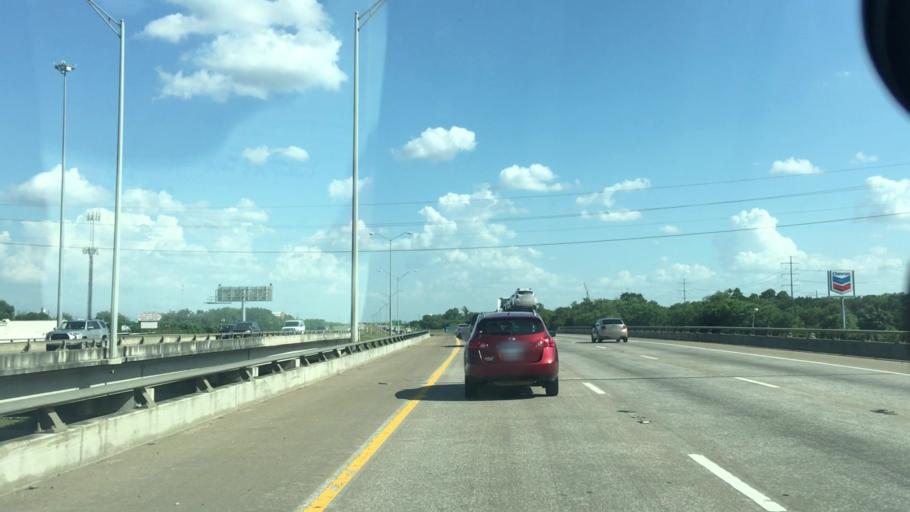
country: US
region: Texas
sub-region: Dallas County
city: Dallas
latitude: 32.7250
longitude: -96.7625
